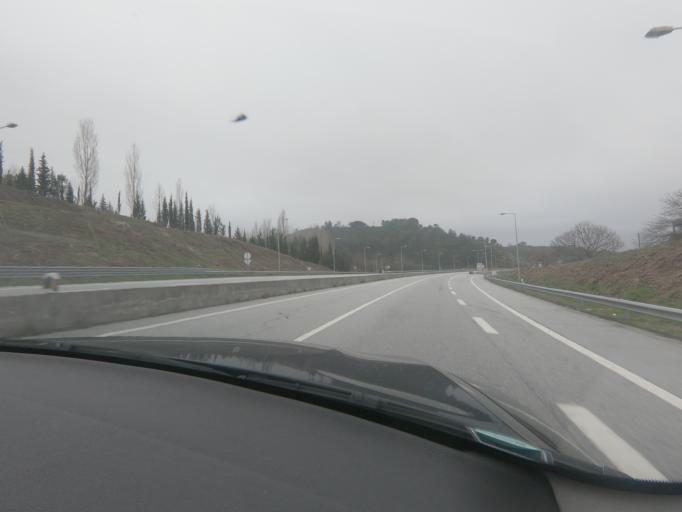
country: PT
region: Viseu
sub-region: Viseu
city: Viseu
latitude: 40.6152
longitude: -7.9636
